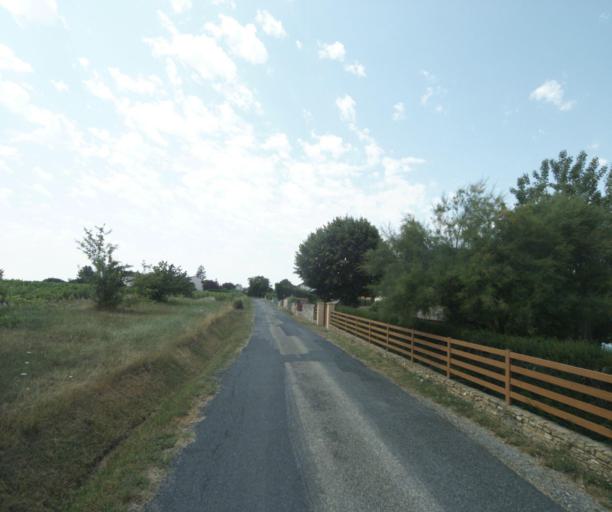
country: FR
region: Rhone-Alpes
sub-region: Departement du Rhone
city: Saint-Germain-Nuelles
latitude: 45.8478
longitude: 4.6234
